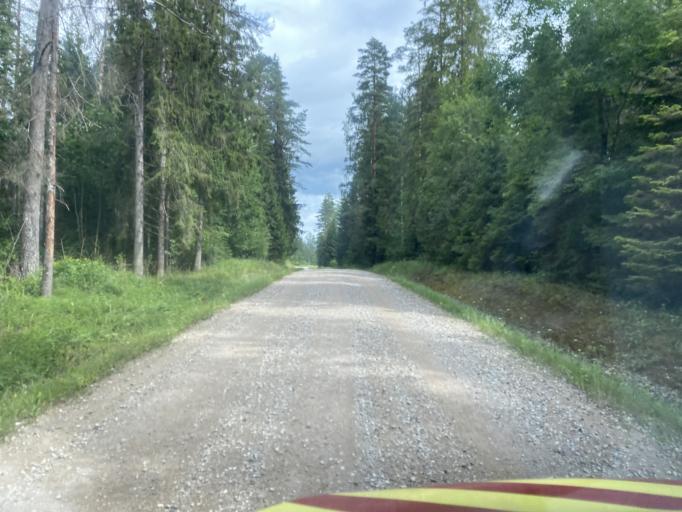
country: EE
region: Valgamaa
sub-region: Torva linn
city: Torva
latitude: 57.9444
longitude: 25.9324
